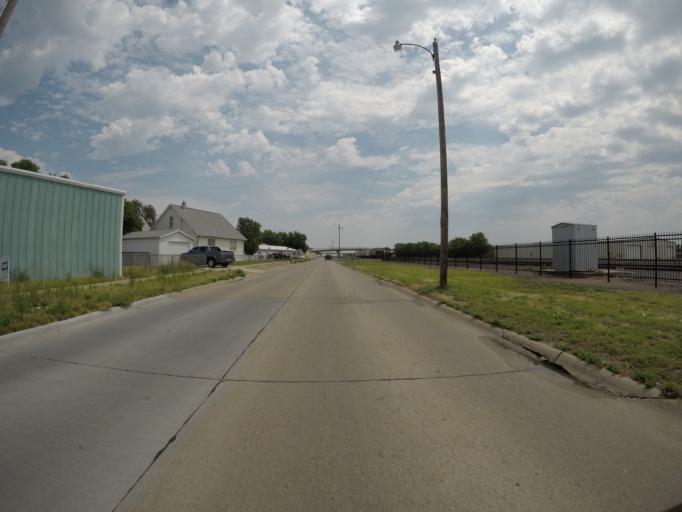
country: US
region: Nebraska
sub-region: Buffalo County
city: Kearney
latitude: 40.6963
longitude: -99.0769
